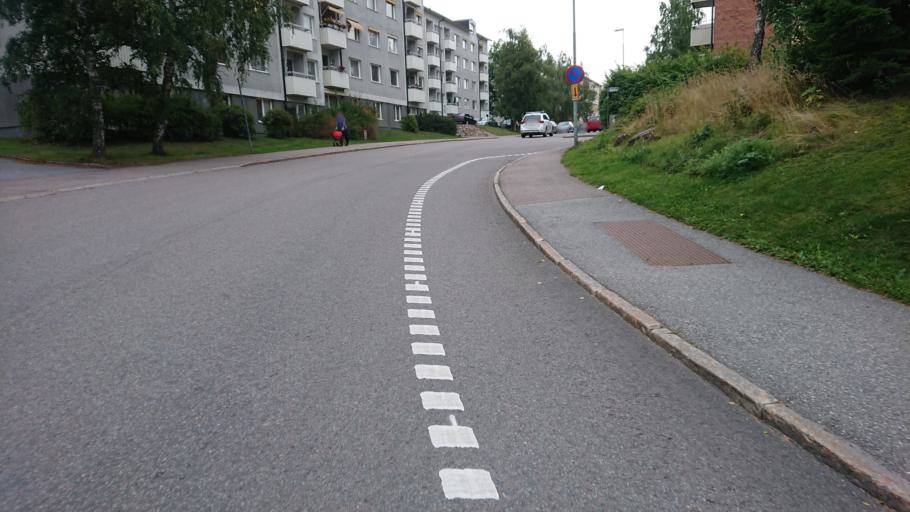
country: SE
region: Uppsala
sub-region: Uppsala Kommun
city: Uppsala
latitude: 59.8426
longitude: 17.6023
